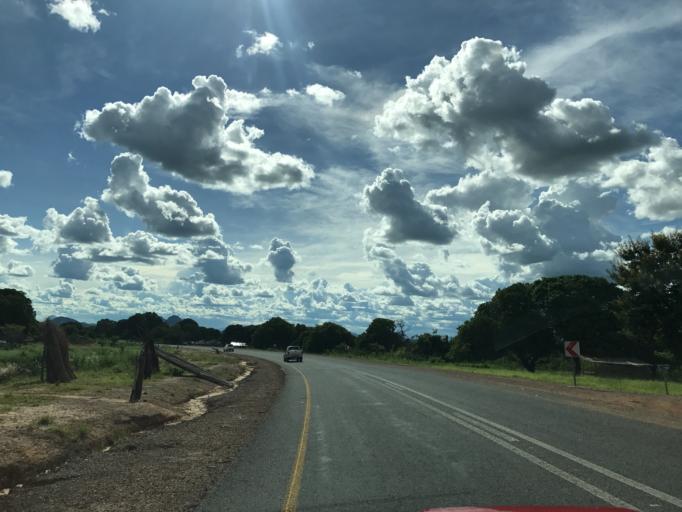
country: MZ
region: Nampula
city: Nampula
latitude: -14.9992
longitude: 39.0212
